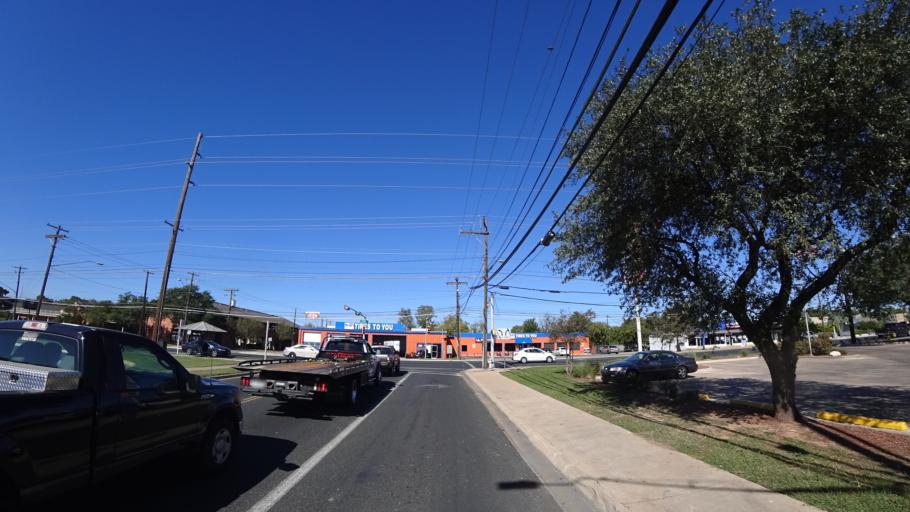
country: US
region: Texas
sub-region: Travis County
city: Austin
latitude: 30.3302
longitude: -97.7231
